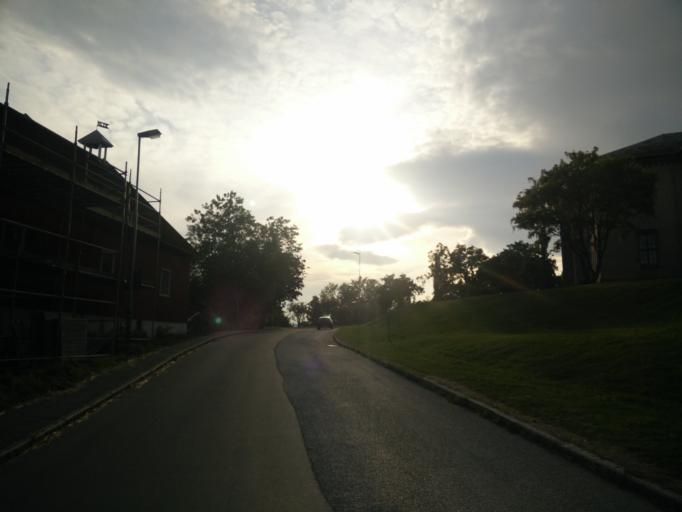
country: NO
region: Sor-Trondelag
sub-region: Trondheim
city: Trondheim
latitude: 63.4388
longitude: 10.4853
